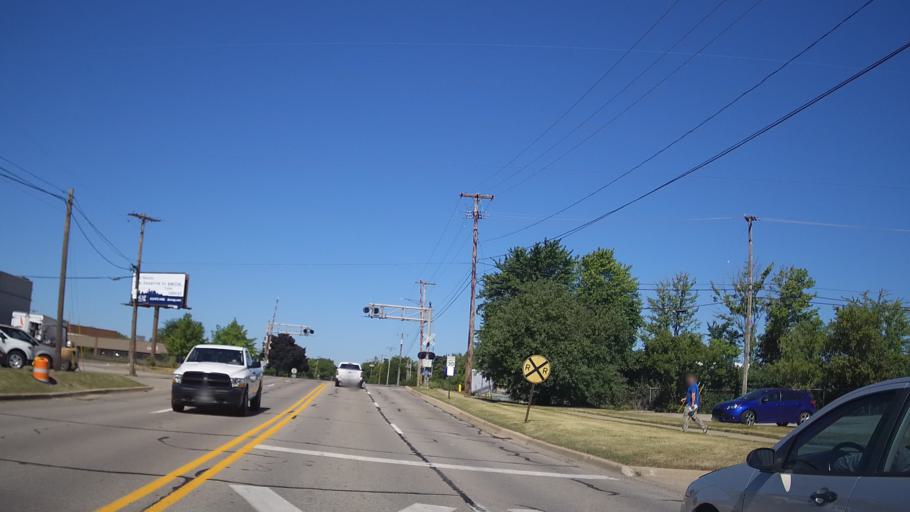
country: US
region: Michigan
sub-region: Macomb County
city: Fraser
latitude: 42.5316
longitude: -82.9425
